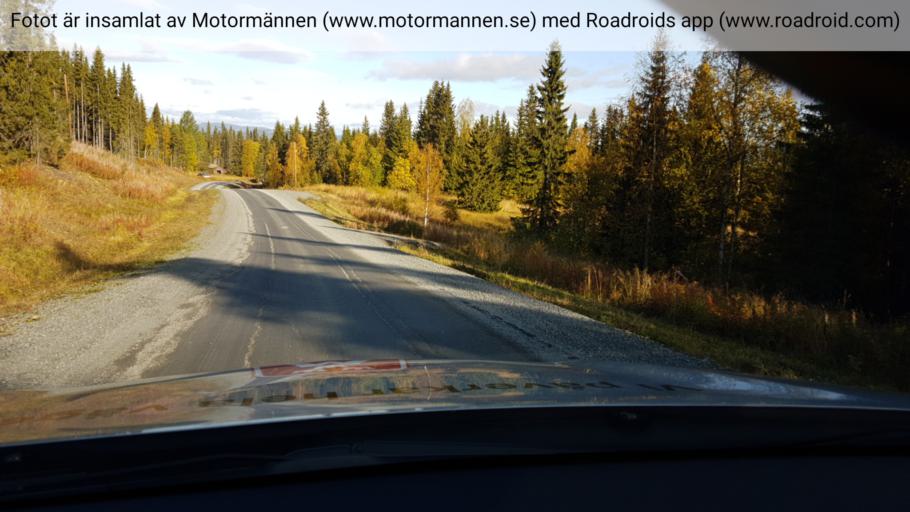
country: SE
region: Vaesterbotten
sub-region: Vilhelmina Kommun
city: Sjoberg
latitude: 64.7865
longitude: 15.9779
